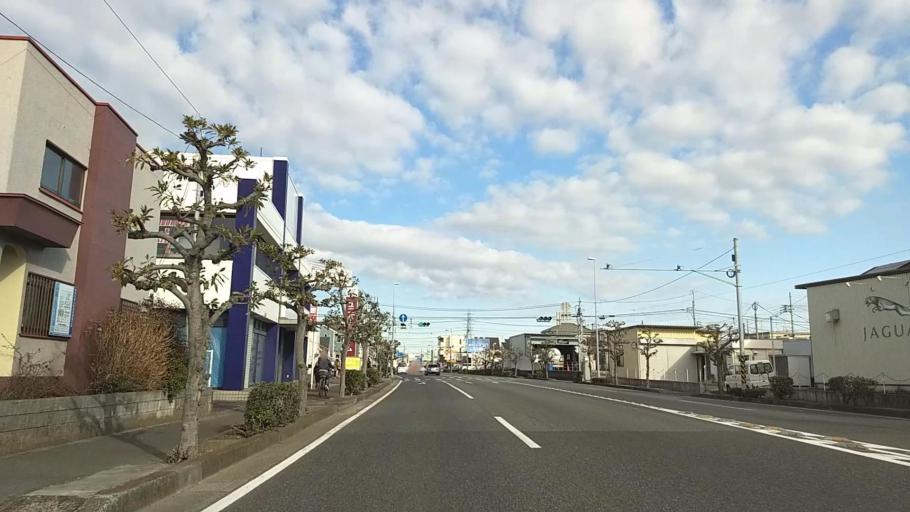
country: JP
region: Kanagawa
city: Hiratsuka
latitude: 35.3498
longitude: 139.3564
